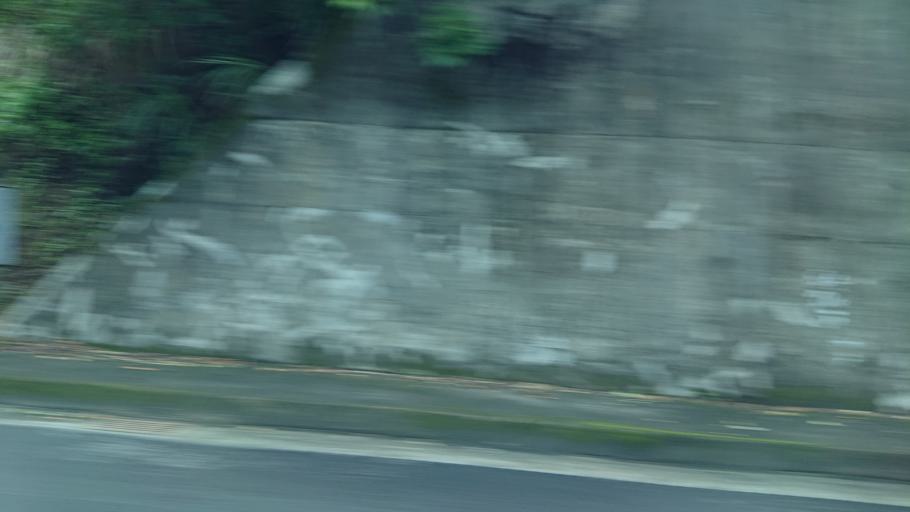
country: TW
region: Taiwan
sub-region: Keelung
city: Keelung
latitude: 25.1204
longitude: 121.8180
